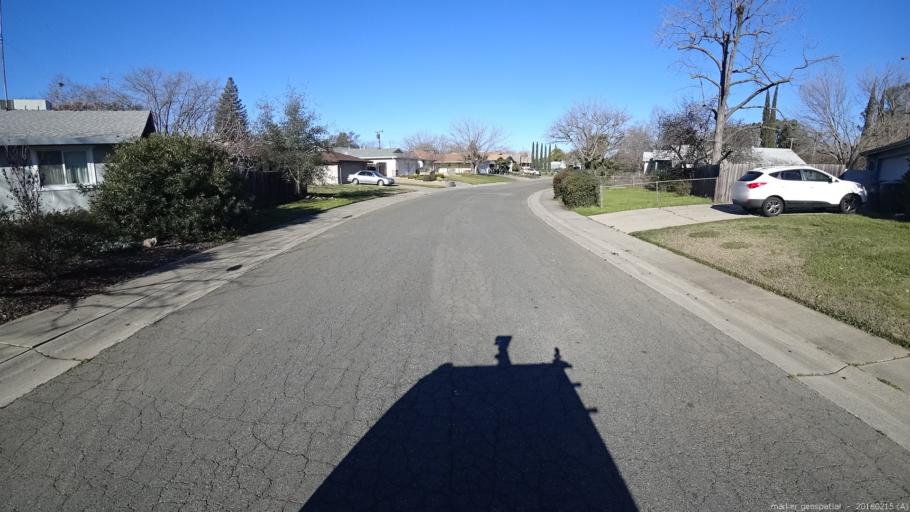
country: US
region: California
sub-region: Sacramento County
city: Foothill Farms
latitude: 38.6657
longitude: -121.3196
